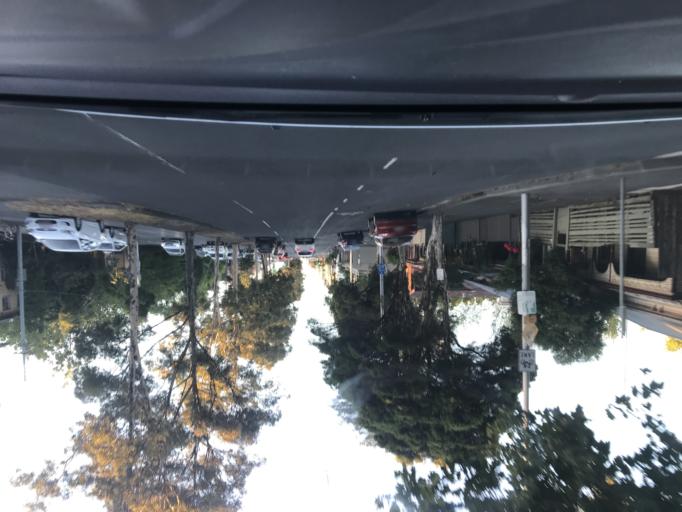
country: AU
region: Victoria
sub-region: Melbourne
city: North Melbourne
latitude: -37.7992
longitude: 144.9489
